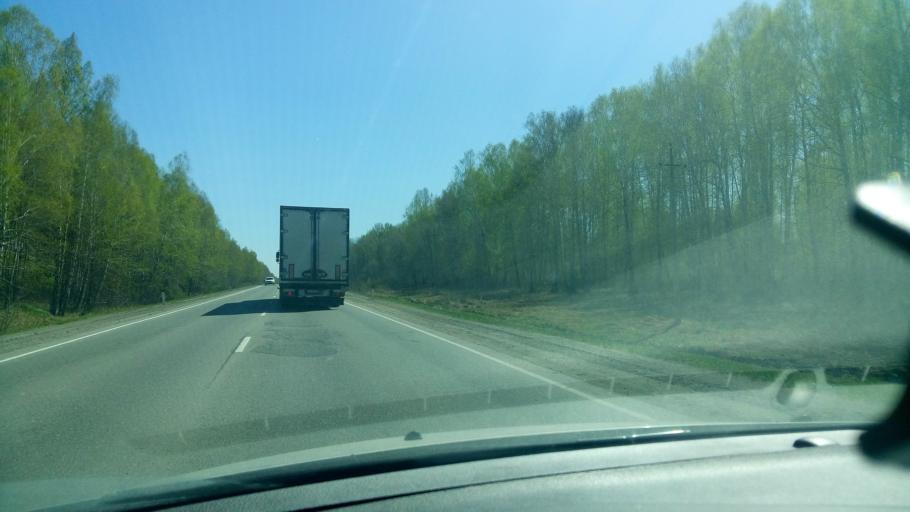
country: RU
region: Sverdlovsk
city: Bogdanovich
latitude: 56.7539
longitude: 62.1637
